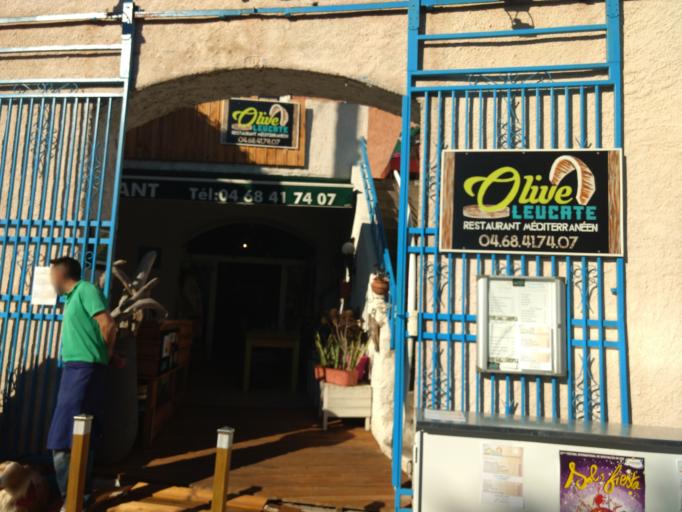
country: FR
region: Languedoc-Roussillon
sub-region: Departement de l'Aude
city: Leucate
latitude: 42.9091
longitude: 3.0307
